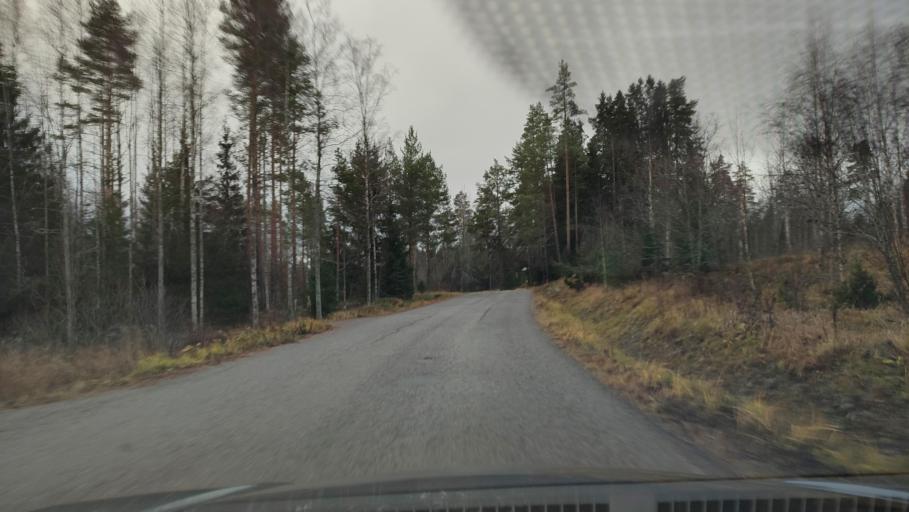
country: FI
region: Southern Ostrobothnia
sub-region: Suupohja
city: Karijoki
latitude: 62.1396
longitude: 21.5727
